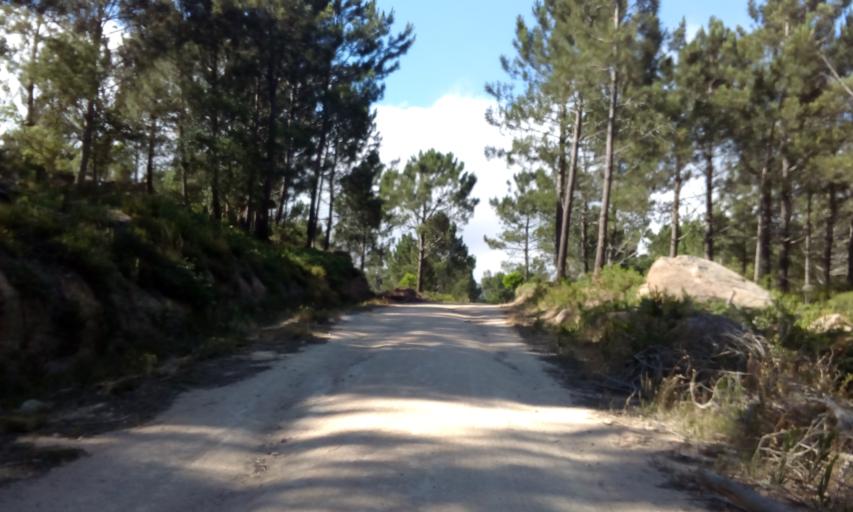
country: PT
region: Lisbon
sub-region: Cascais
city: Alcabideche
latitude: 38.7616
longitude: -9.4310
